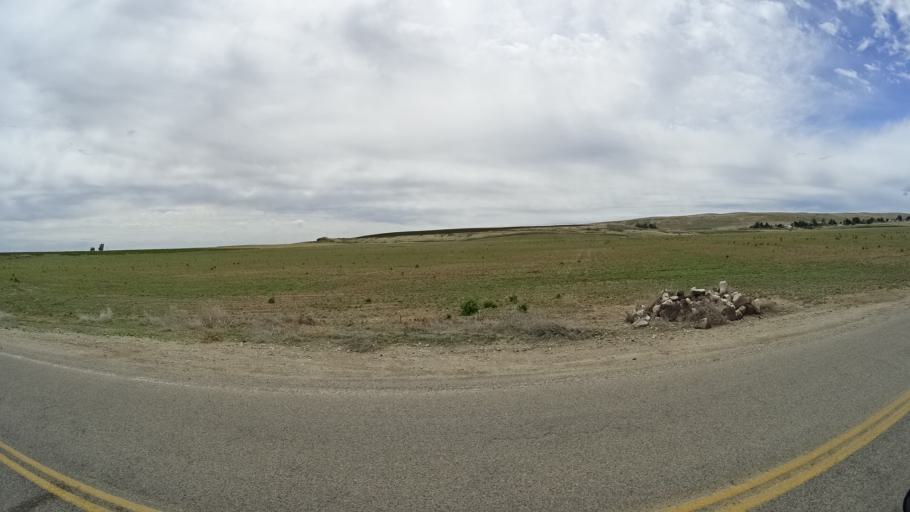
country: US
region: Idaho
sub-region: Ada County
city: Kuna
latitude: 43.4700
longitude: -116.4380
